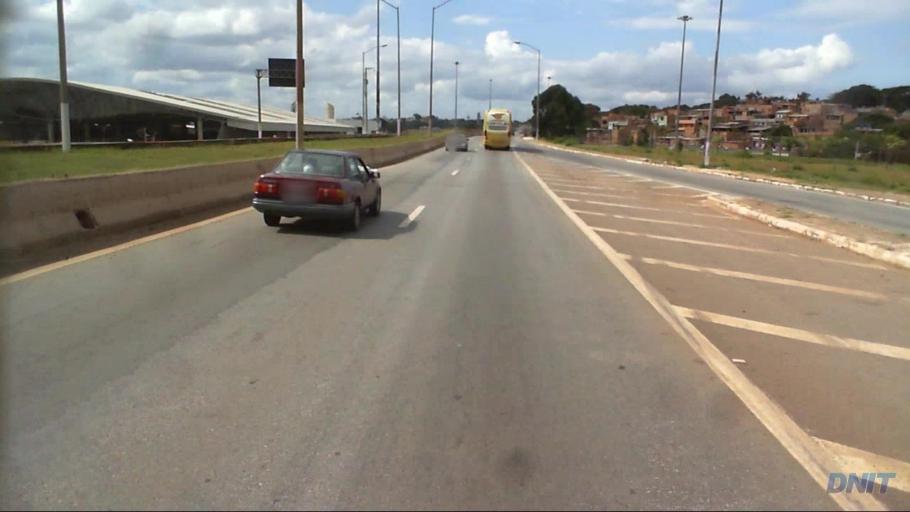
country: BR
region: Minas Gerais
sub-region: Belo Horizonte
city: Belo Horizonte
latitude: -19.8658
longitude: -43.9288
